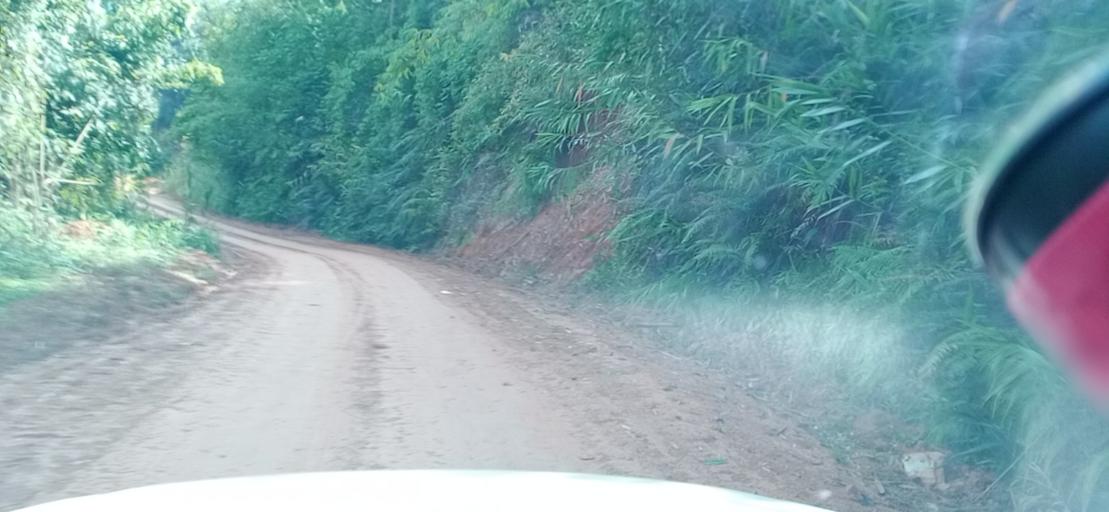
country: TH
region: Changwat Bueng Kan
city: Pak Khat
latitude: 18.6367
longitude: 103.2518
